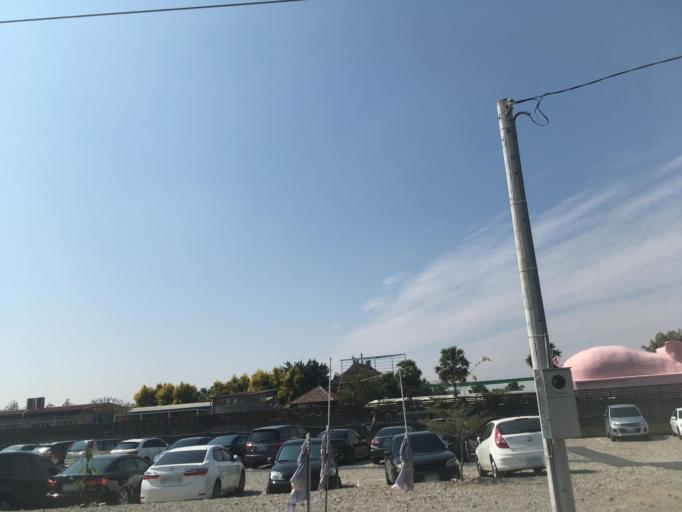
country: TW
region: Taiwan
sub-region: Chiayi
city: Jiayi Shi
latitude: 23.5547
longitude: 120.4127
